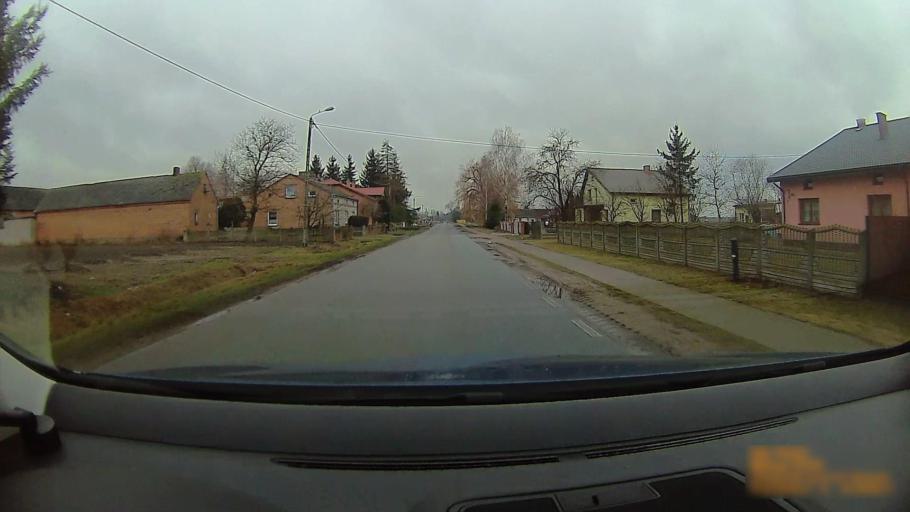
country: PL
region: Greater Poland Voivodeship
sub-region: Powiat koninski
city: Rychwal
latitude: 52.0955
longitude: 18.1626
